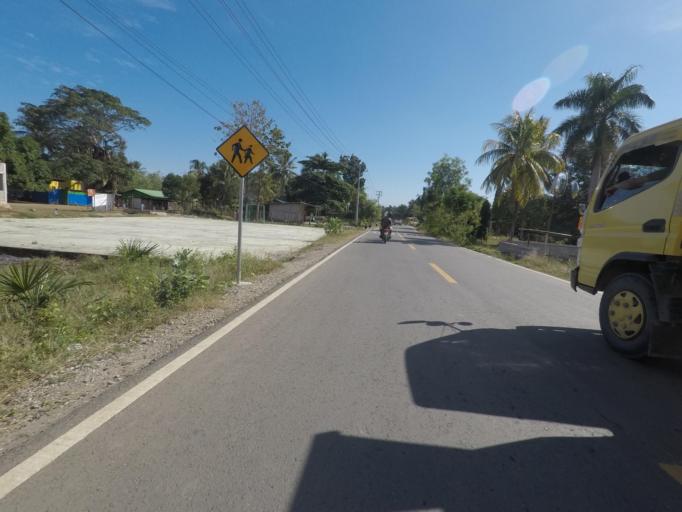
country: TL
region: Bobonaro
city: Maliana
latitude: -8.9670
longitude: 125.2174
